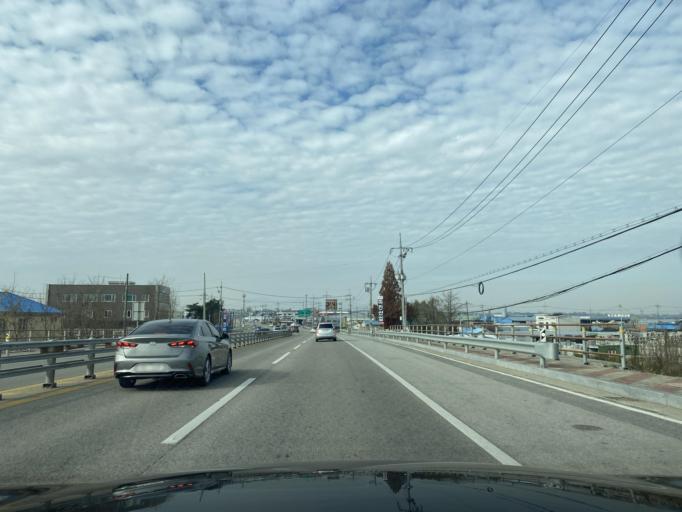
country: KR
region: Chungcheongnam-do
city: Yesan
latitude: 36.6846
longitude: 126.8185
